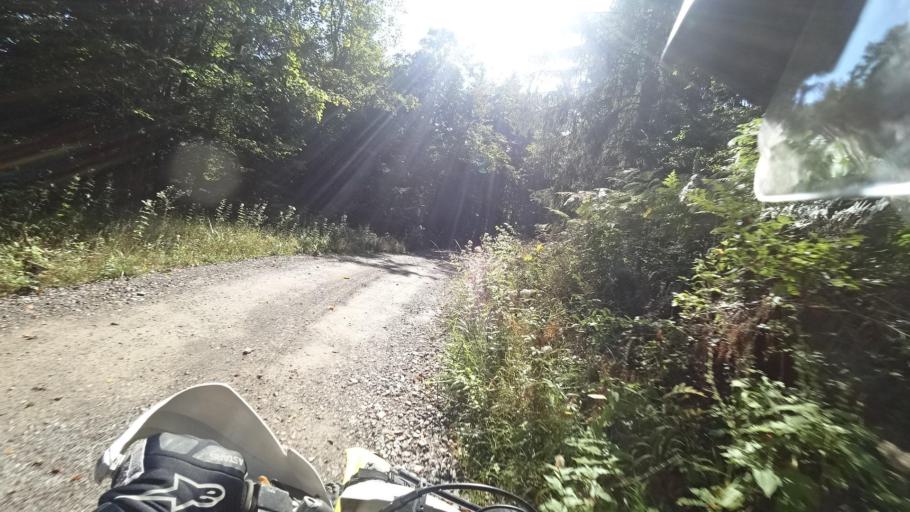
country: HR
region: Karlovacka
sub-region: Grad Ogulin
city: Ogulin
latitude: 45.2558
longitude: 15.1167
